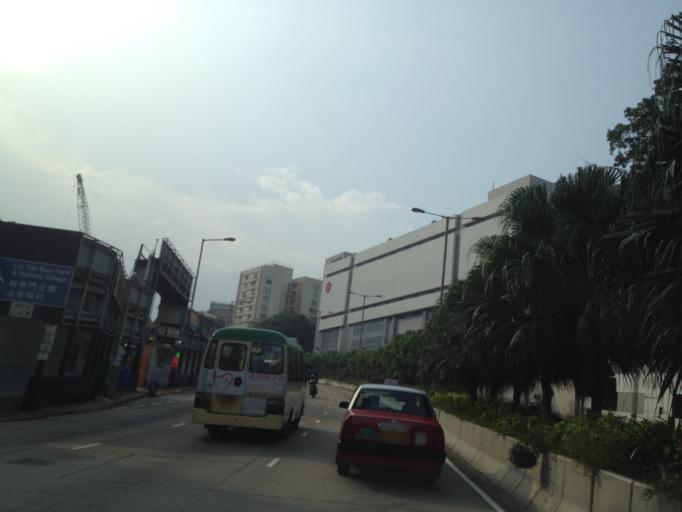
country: HK
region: Wanchai
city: Wan Chai
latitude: 22.2751
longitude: 114.2309
